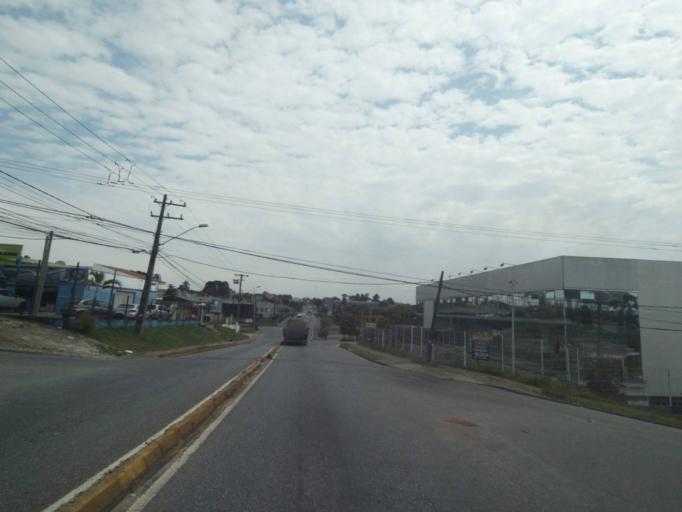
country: BR
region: Parana
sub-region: Pinhais
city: Pinhais
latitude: -25.3950
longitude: -49.2093
